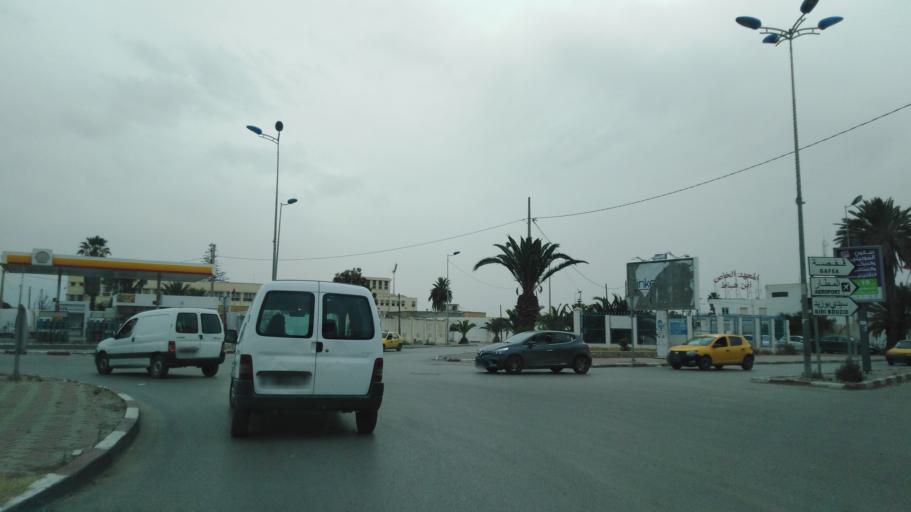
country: TN
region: Safaqis
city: Sfax
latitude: 34.7339
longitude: 10.7514
